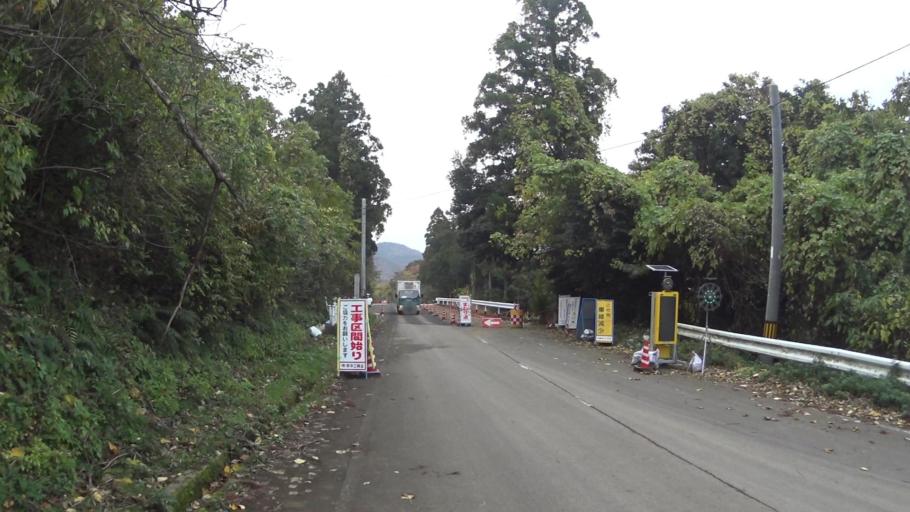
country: JP
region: Kyoto
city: Maizuru
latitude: 35.5685
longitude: 135.4616
